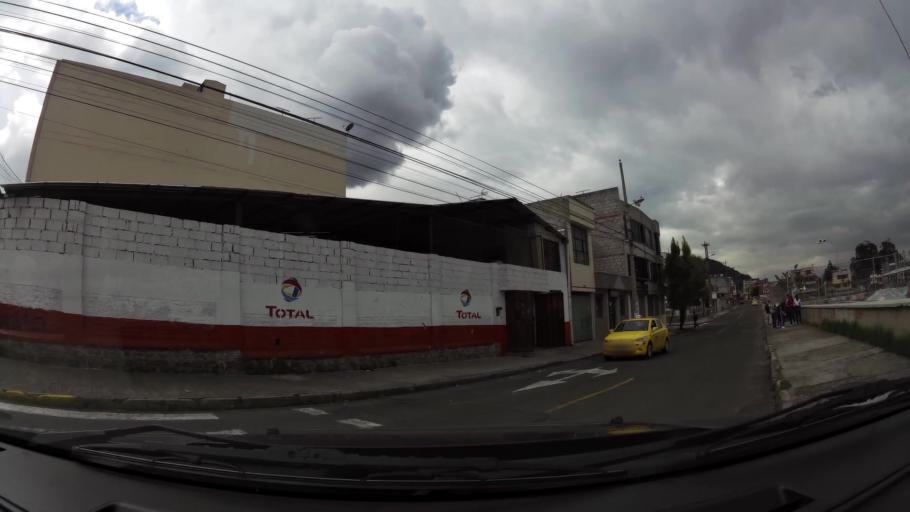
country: EC
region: Pichincha
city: Quito
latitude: -0.2452
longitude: -78.5274
